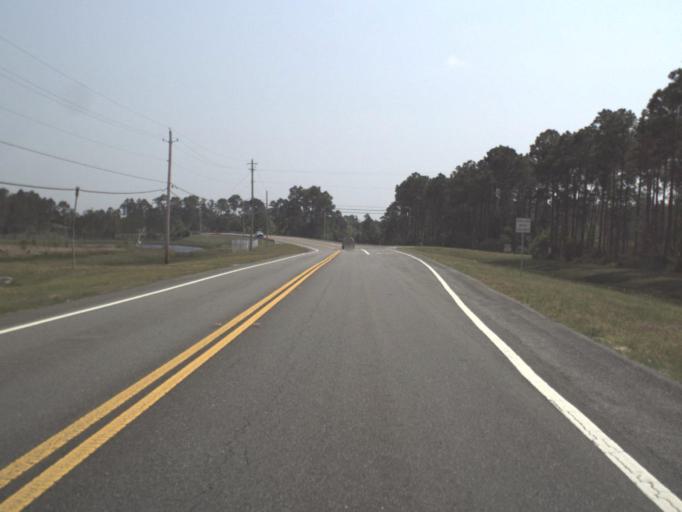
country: US
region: Florida
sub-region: Santa Rosa County
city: Bagdad
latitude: 30.5179
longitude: -87.0874
